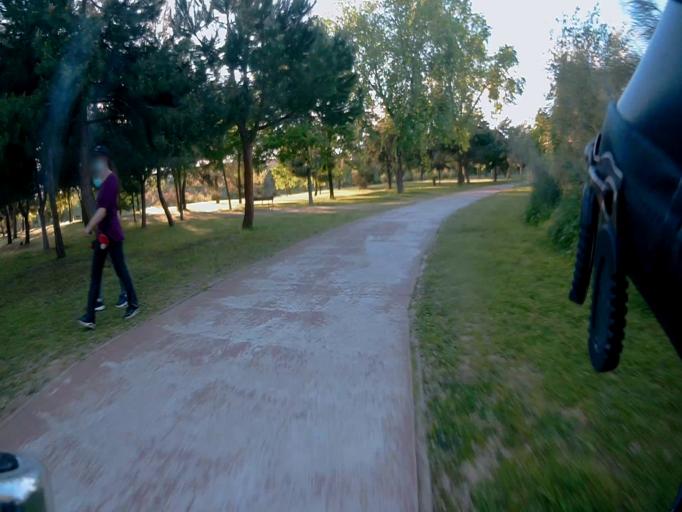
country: ES
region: Madrid
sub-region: Provincia de Madrid
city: Fuenlabrada
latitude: 40.3143
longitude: -3.7937
